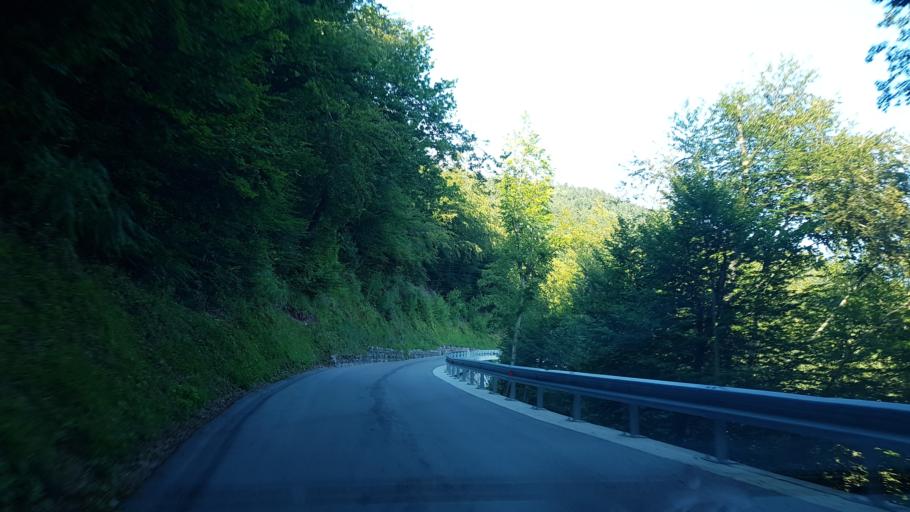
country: SI
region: Idrija
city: Spodnja Idrija
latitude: 46.0755
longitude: 14.0025
